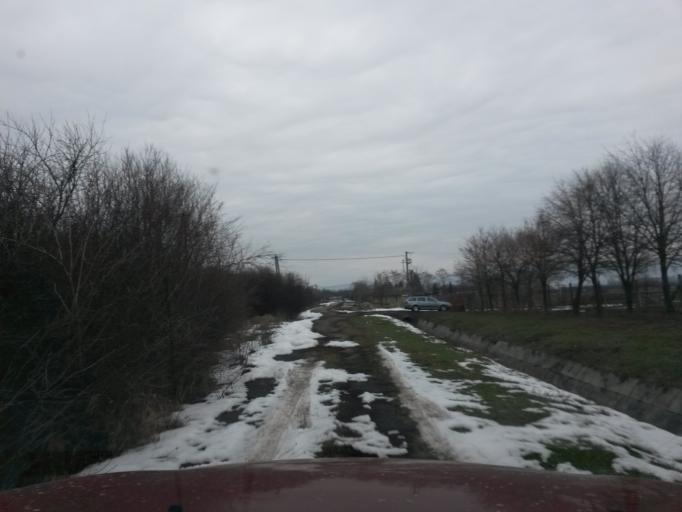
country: SK
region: Kosicky
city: Vinne
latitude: 48.7442
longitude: 22.0232
